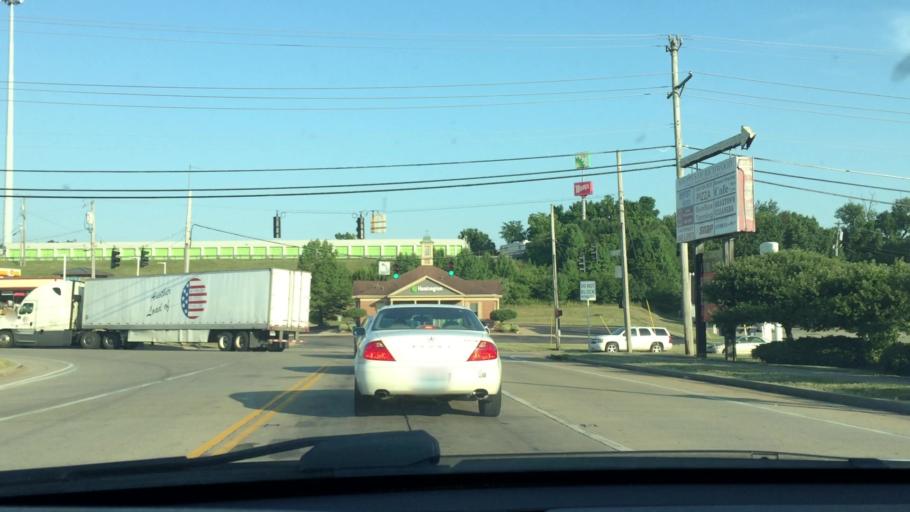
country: US
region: Kentucky
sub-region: Boone County
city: Walton
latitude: 38.9169
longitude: -84.6328
